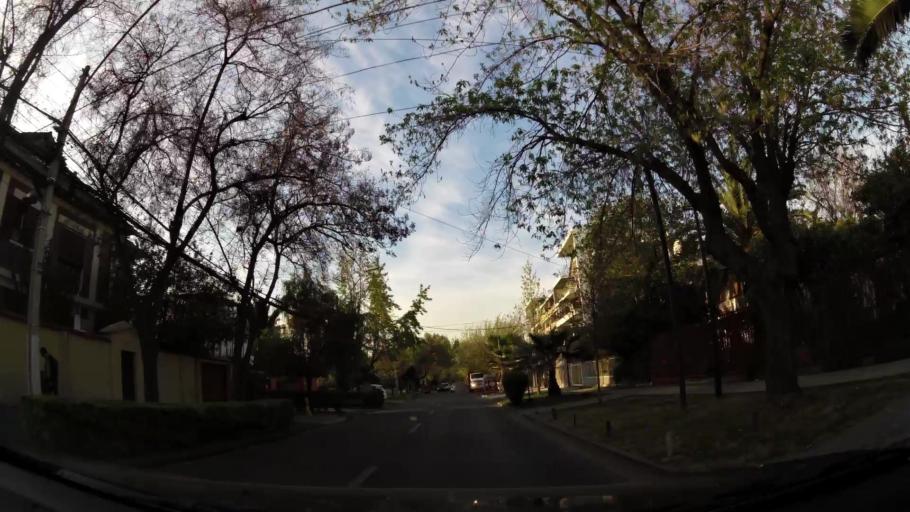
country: CL
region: Santiago Metropolitan
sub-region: Provincia de Santiago
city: Villa Presidente Frei, Nunoa, Santiago, Chile
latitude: -33.4487
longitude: -70.5768
